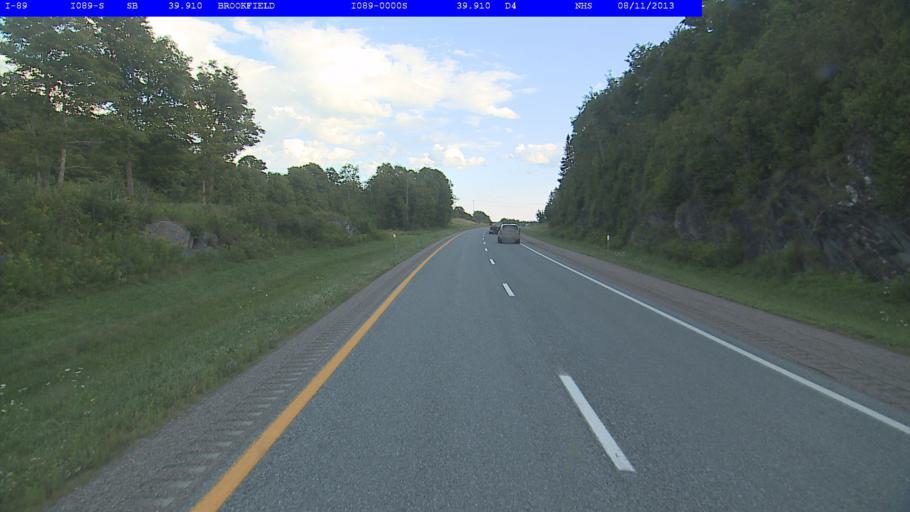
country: US
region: Vermont
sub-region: Orange County
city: Williamstown
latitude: 44.0728
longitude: -72.6093
